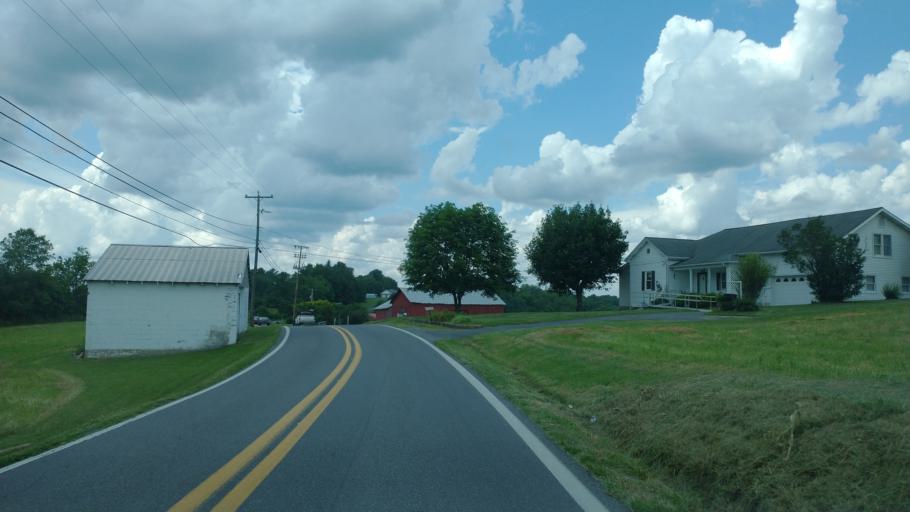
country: US
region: West Virginia
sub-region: Mercer County
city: Athens
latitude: 37.4061
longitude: -81.0591
